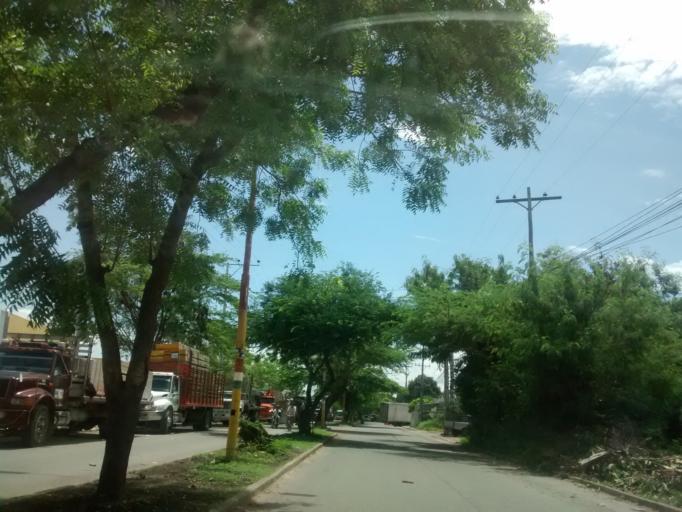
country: CO
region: Cundinamarca
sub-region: Girardot
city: Girardot City
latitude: 4.3081
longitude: -74.7951
